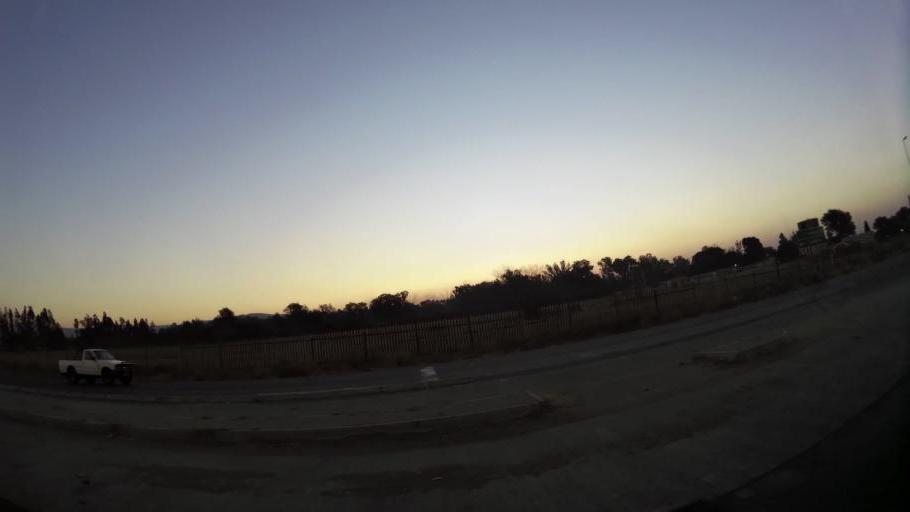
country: ZA
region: North-West
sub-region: Bojanala Platinum District Municipality
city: Rustenburg
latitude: -25.6403
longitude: 27.2630
